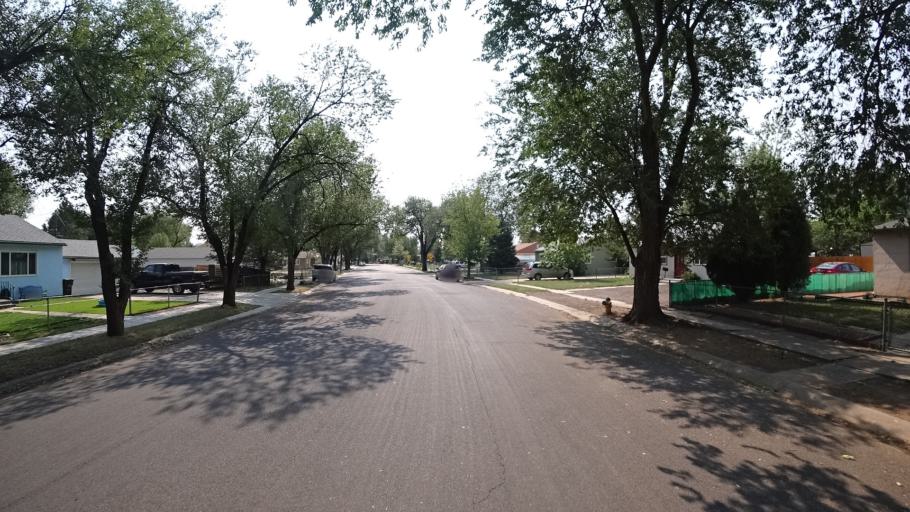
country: US
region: Colorado
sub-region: El Paso County
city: Colorado Springs
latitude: 38.8047
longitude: -104.8165
